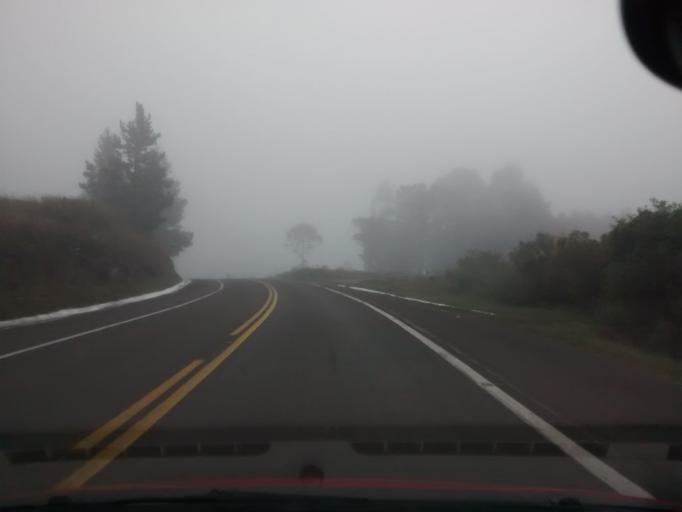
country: BR
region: Rio Grande do Sul
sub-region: Vacaria
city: Vacaria
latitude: -28.2938
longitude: -50.8020
